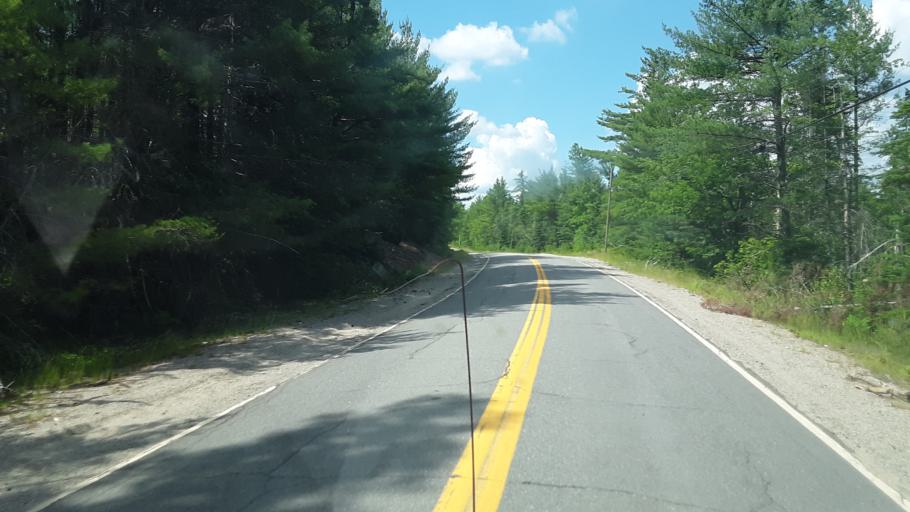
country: US
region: Maine
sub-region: Washington County
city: Machias
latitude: 44.8851
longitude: -67.6220
